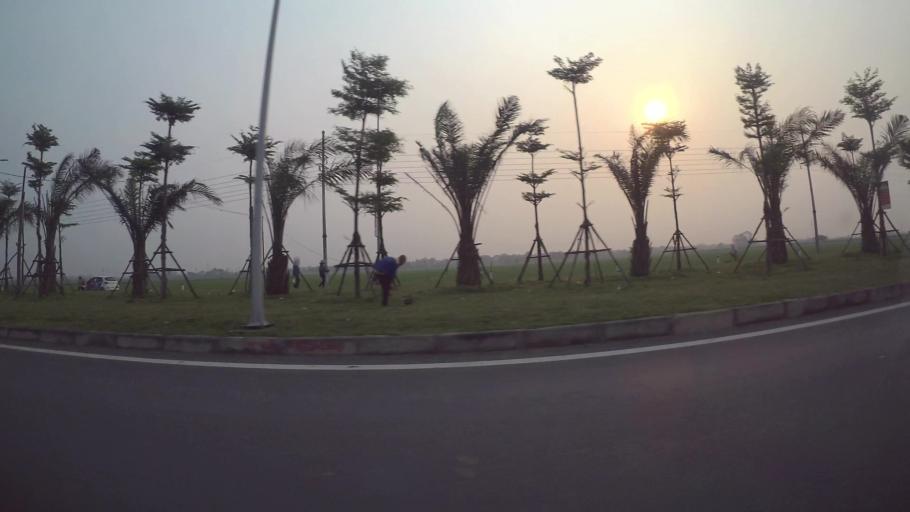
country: VN
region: Ha Noi
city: Kim Bai
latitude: 20.8881
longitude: 105.7962
